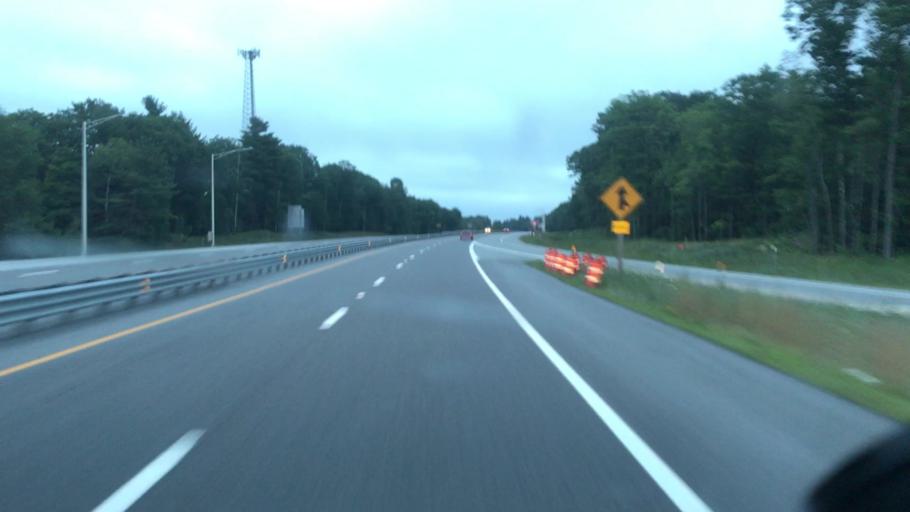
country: US
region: Maine
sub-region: Androscoggin County
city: Lewiston
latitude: 44.0716
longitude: -70.1813
